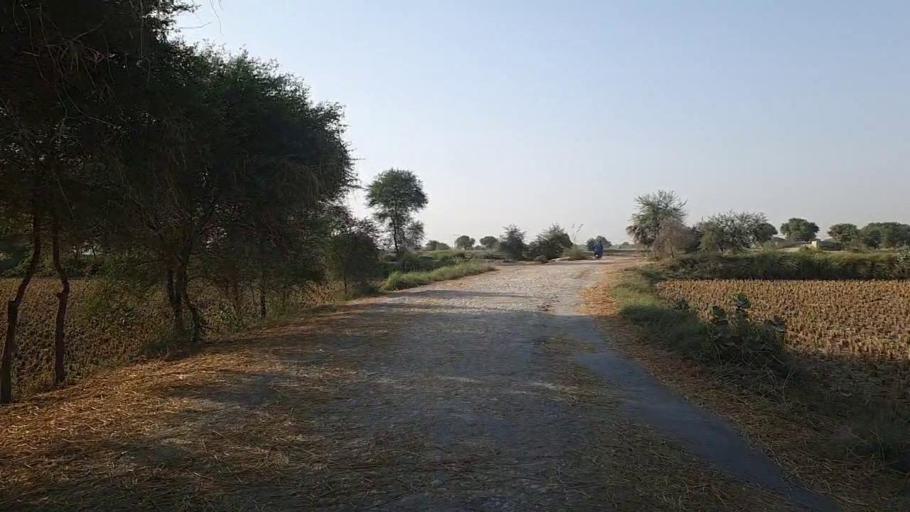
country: PK
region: Sindh
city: Kashmor
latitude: 28.4070
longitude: 69.4136
